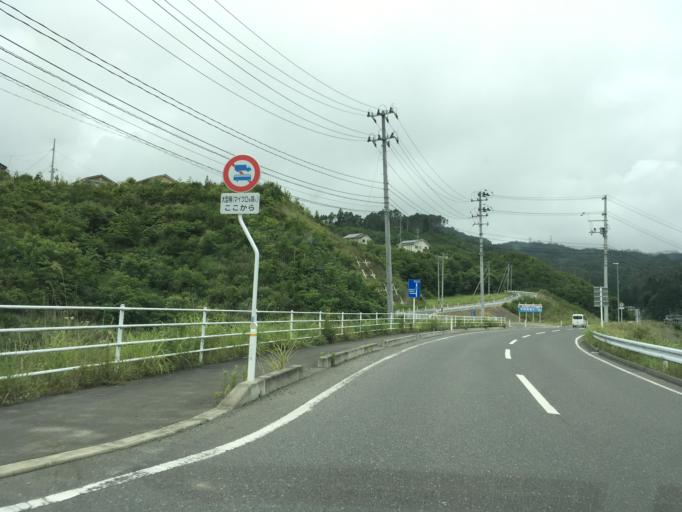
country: JP
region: Iwate
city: Ofunato
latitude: 38.9026
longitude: 141.6238
